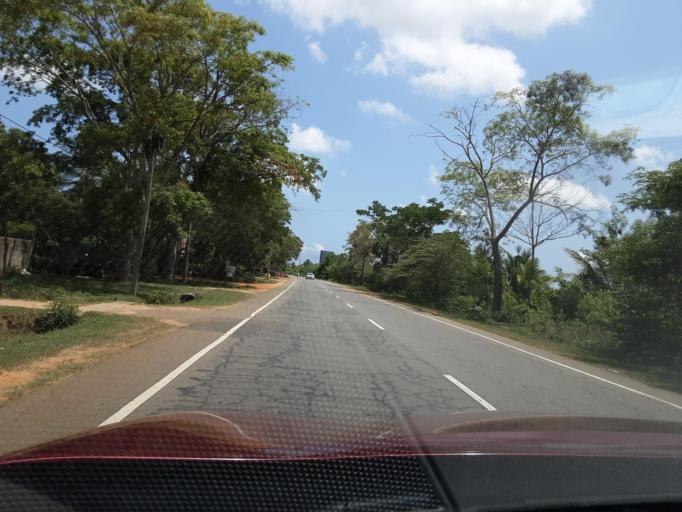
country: LK
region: Southern
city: Tangalla
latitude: 6.2431
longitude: 81.2270
